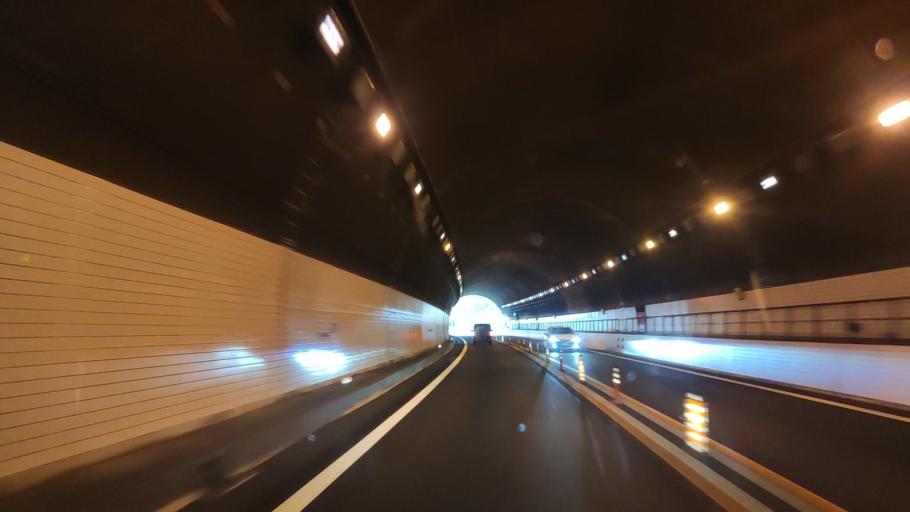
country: JP
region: Tokushima
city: Ikedacho
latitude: 34.0507
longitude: 133.9176
